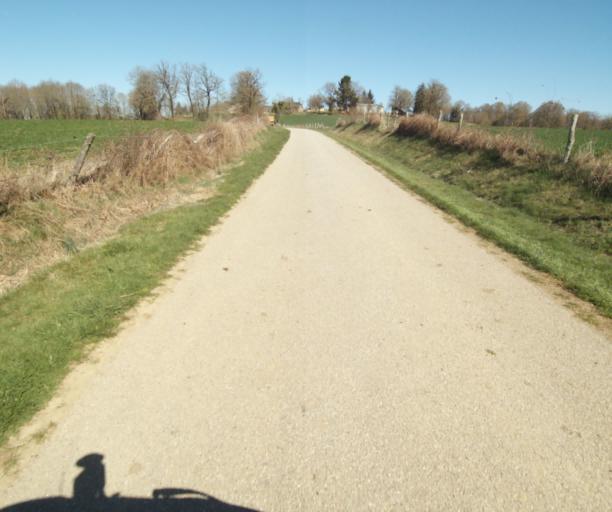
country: FR
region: Limousin
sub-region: Departement de la Correze
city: Chamboulive
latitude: 45.4239
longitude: 1.7218
